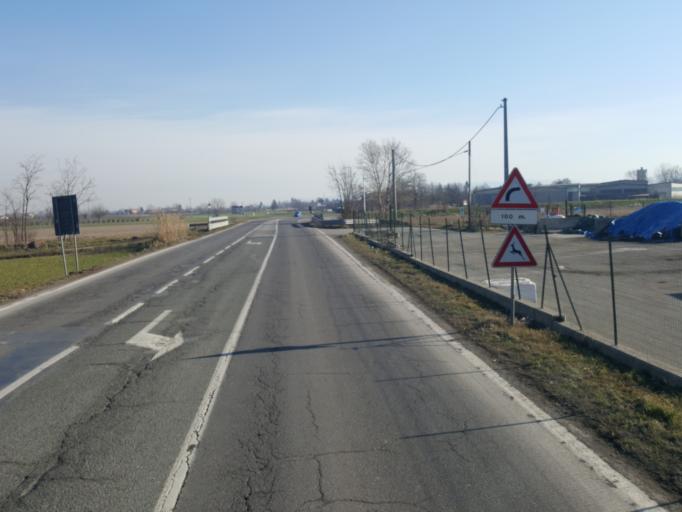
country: IT
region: Piedmont
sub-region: Provincia di Alessandria
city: Viguzzolo
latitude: 44.9071
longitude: 8.9013
